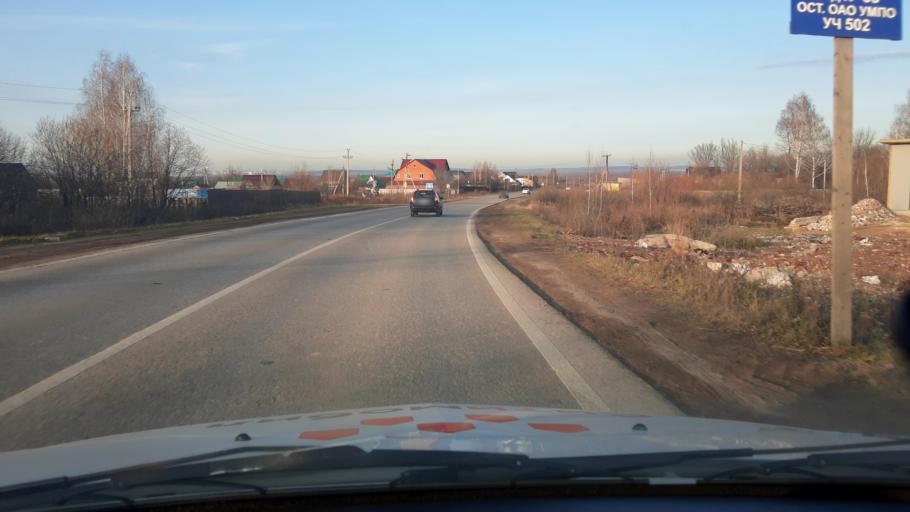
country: RU
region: Bashkortostan
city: Kabakovo
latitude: 54.7085
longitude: 56.1682
